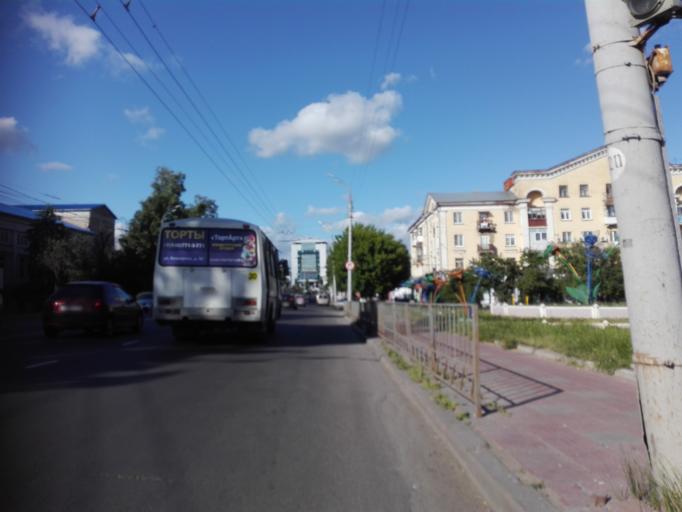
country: RU
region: Orjol
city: Orel
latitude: 52.9784
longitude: 36.1034
